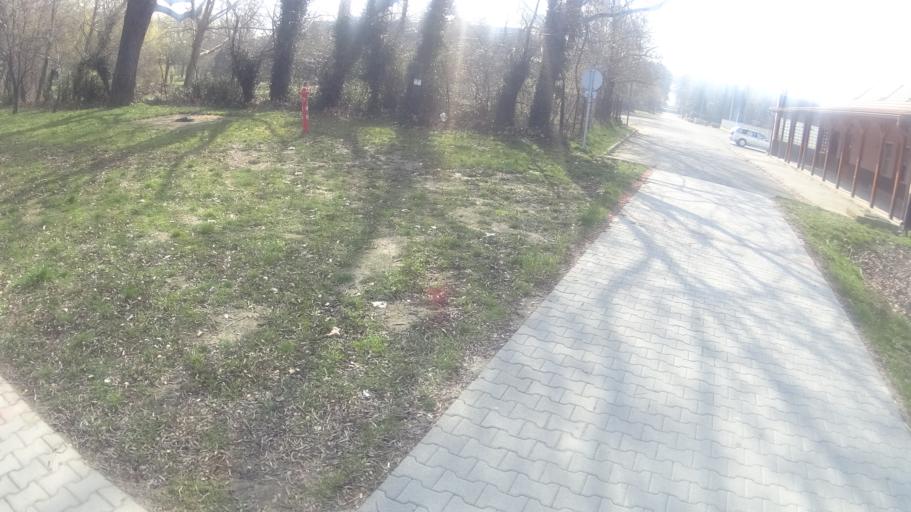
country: HU
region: Somogy
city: Siofok
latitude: 46.9258
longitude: 18.0944
